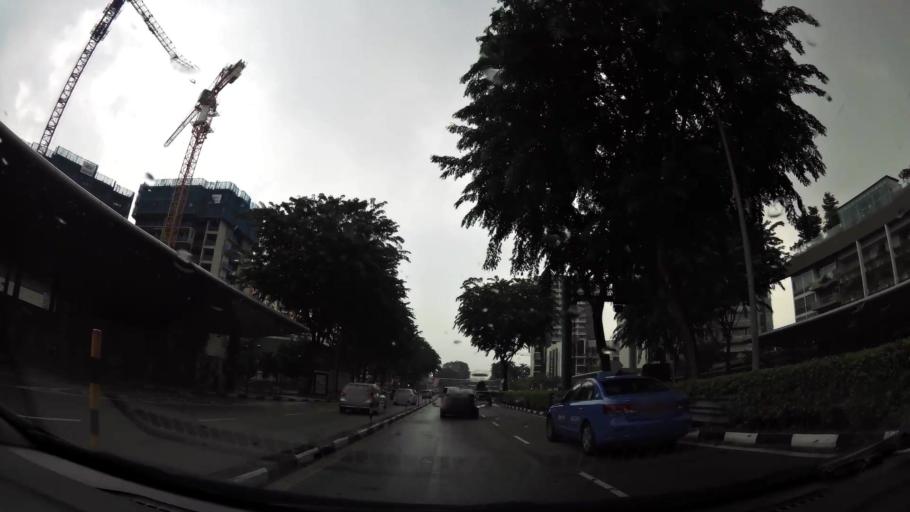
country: SG
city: Singapore
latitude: 1.3312
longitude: 103.8690
